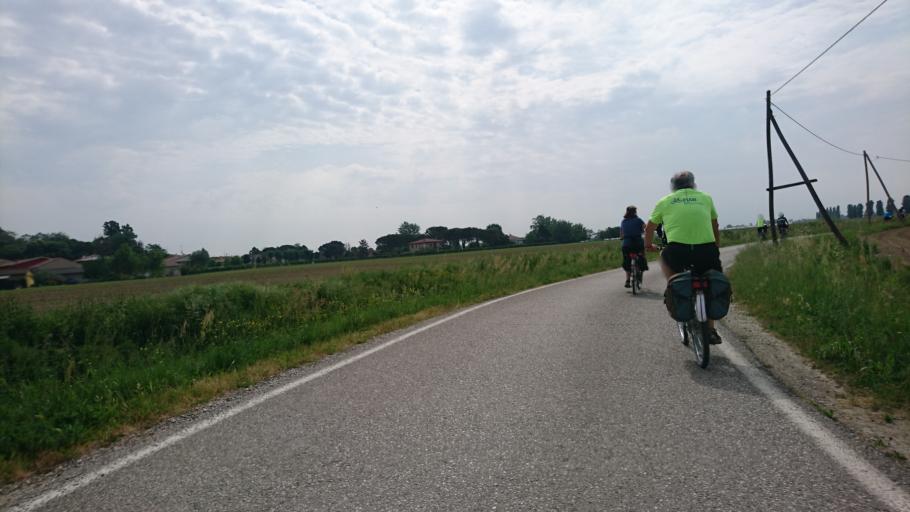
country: IT
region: Veneto
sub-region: Provincia di Padova
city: Pernumia
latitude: 45.2558
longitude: 11.7851
